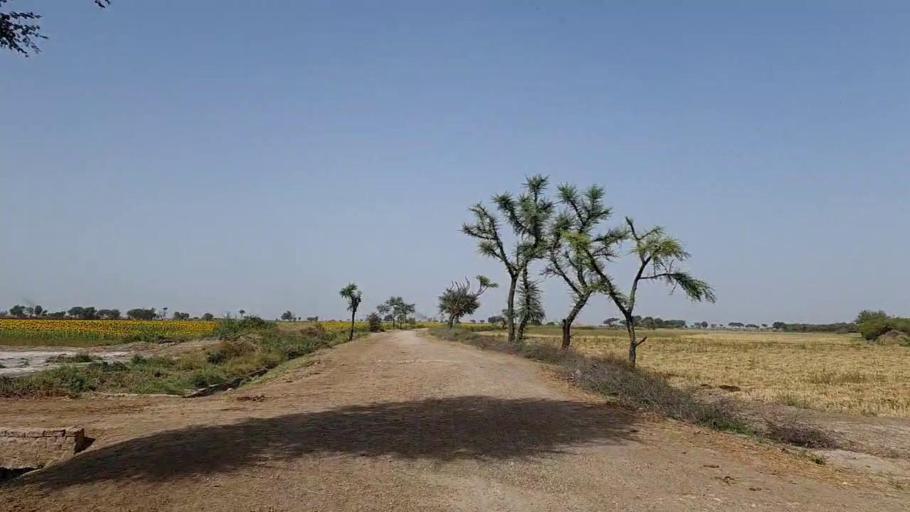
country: PK
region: Sindh
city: Jati
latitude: 24.3431
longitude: 68.3043
